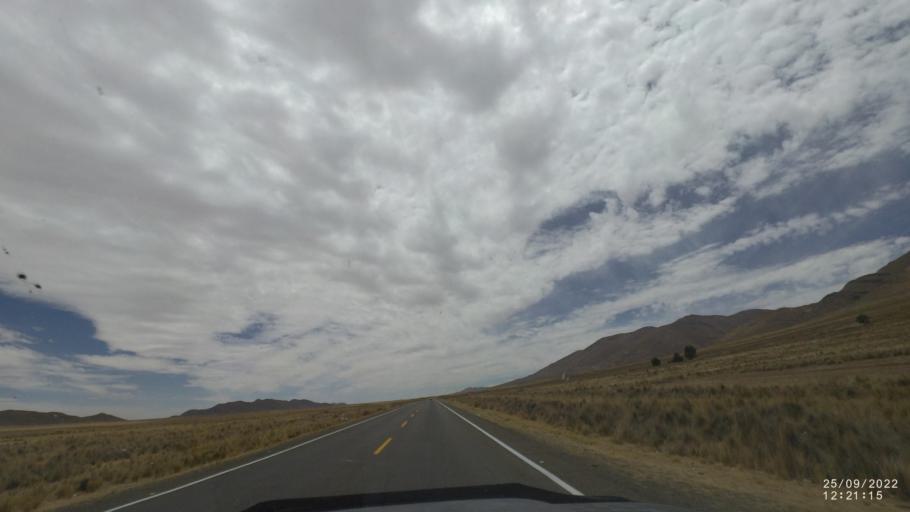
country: BO
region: Oruro
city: Poopo
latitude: -18.4153
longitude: -66.9756
